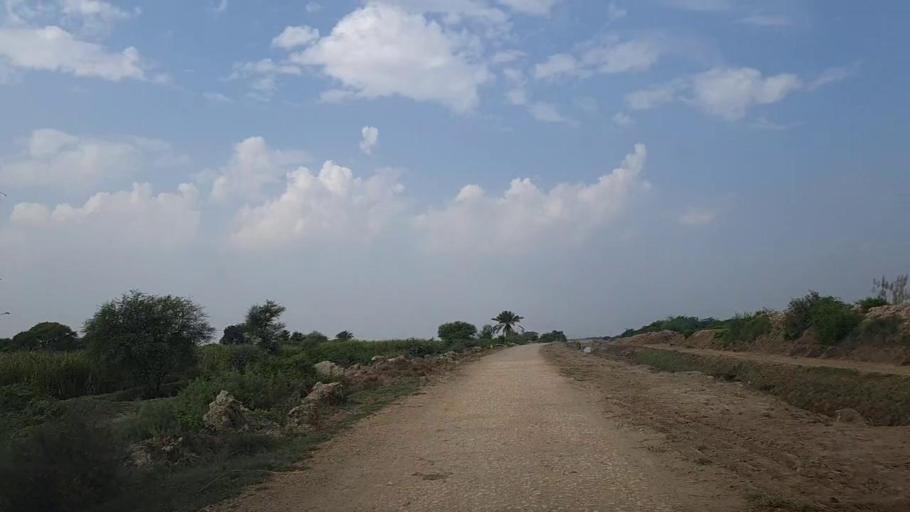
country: PK
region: Sindh
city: Daro Mehar
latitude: 24.7184
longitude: 68.1393
